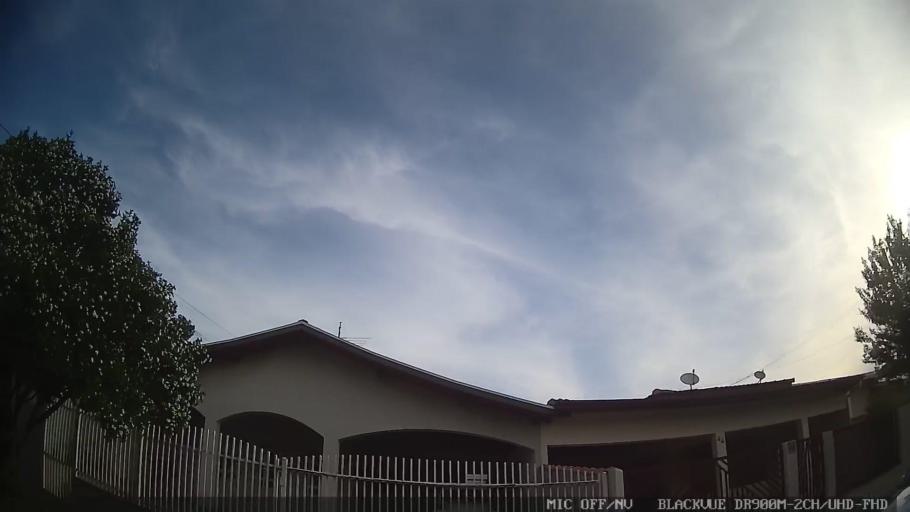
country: BR
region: Sao Paulo
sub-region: Jaguariuna
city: Jaguariuna
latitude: -22.6427
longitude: -47.0516
